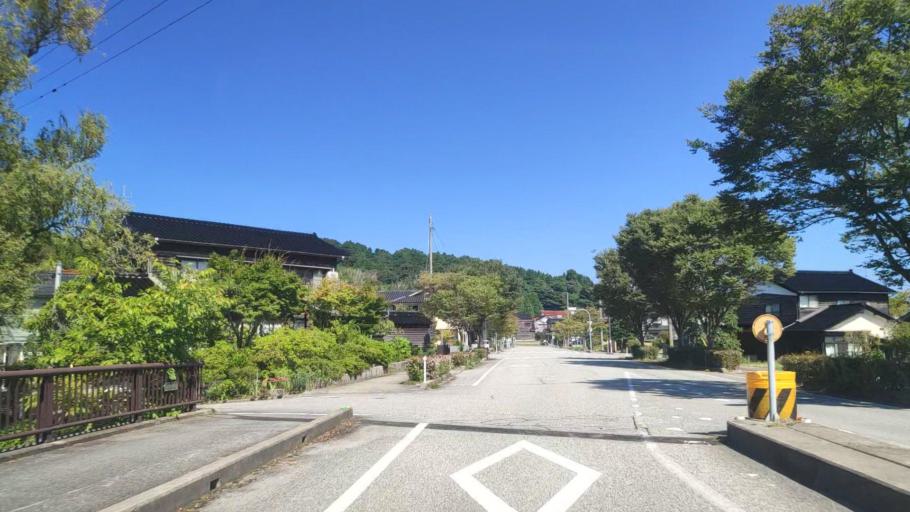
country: JP
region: Ishikawa
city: Nanao
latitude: 37.3931
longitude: 136.8929
